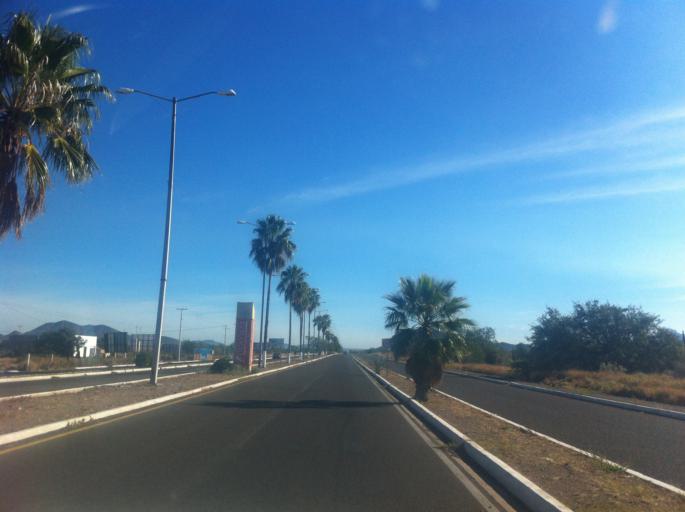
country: MX
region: Sonora
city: Heroica Guaymas
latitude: 27.9674
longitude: -111.0093
